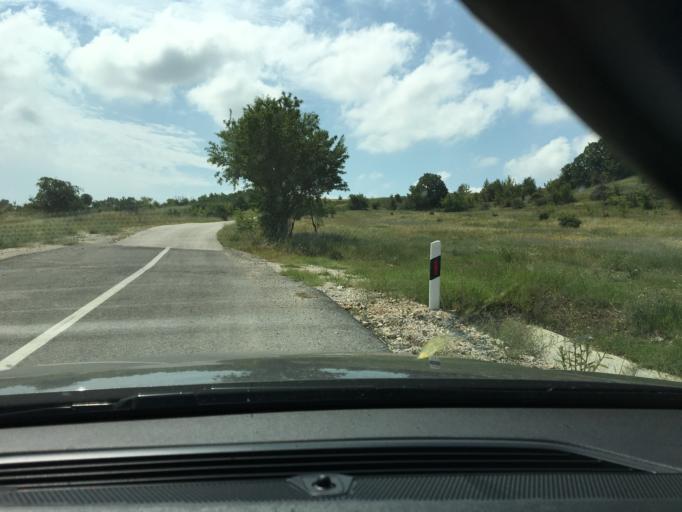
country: MK
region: Sveti Nikole
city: Gorobinci
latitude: 41.9146
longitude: 21.8799
